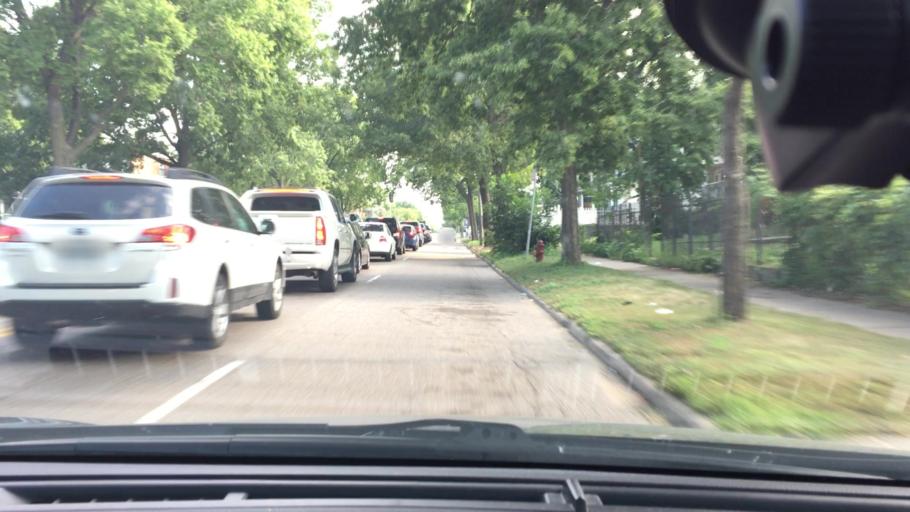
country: US
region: Minnesota
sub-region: Hennepin County
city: Minneapolis
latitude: 44.9531
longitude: -93.2475
